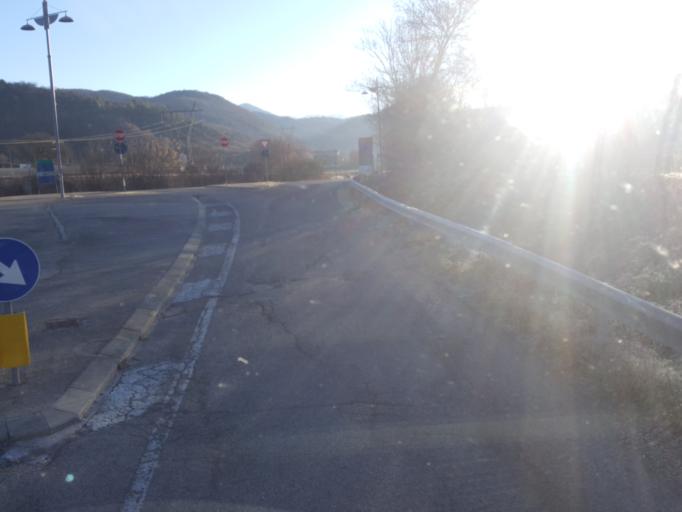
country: IT
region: Latium
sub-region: Provincia di Rieti
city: Labro
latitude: 42.5360
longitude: 12.7737
